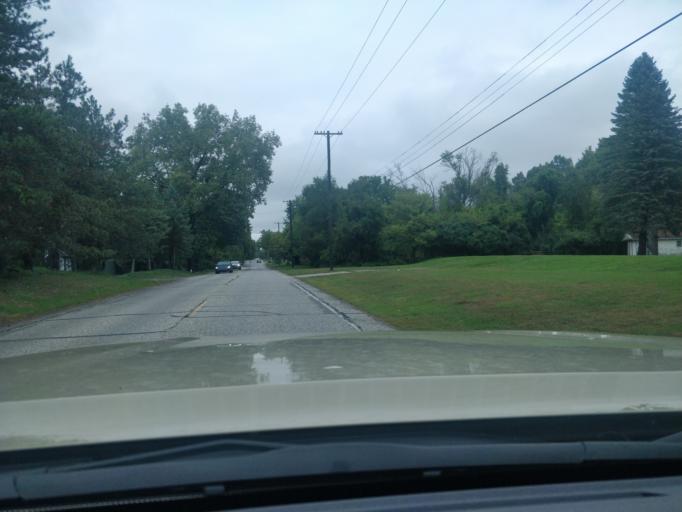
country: US
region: Michigan
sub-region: Wayne County
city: Romulus
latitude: 42.1850
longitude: -83.4187
